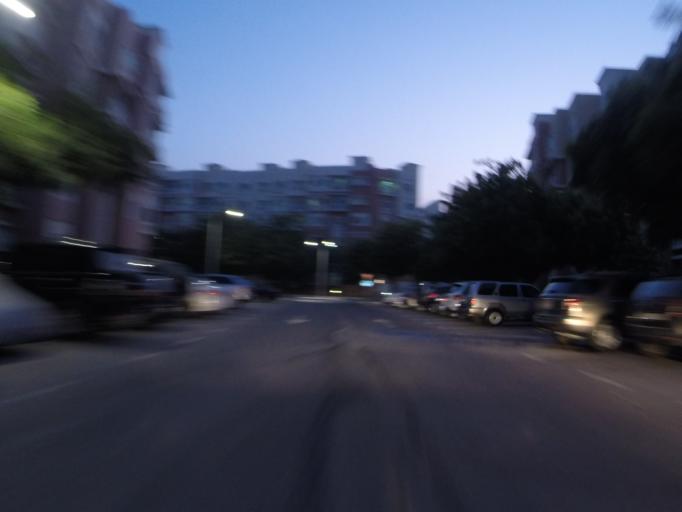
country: AE
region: Dubai
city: Dubai
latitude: 25.0491
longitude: 55.1355
